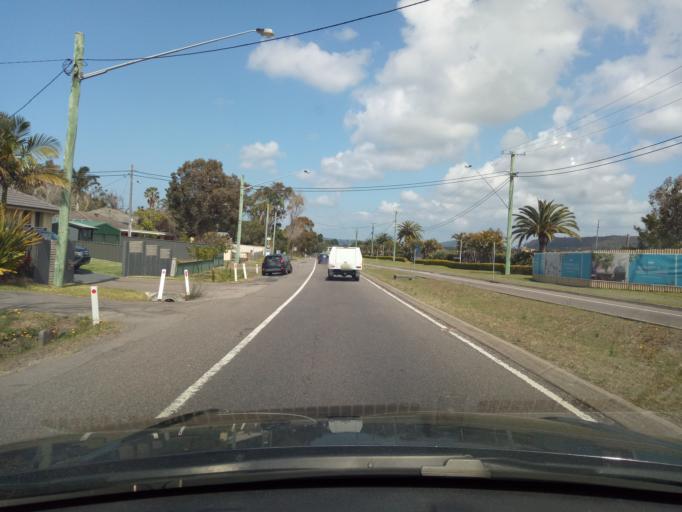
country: AU
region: New South Wales
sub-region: Gosford Shire
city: Forresters Beach
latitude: -33.4017
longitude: 151.4685
